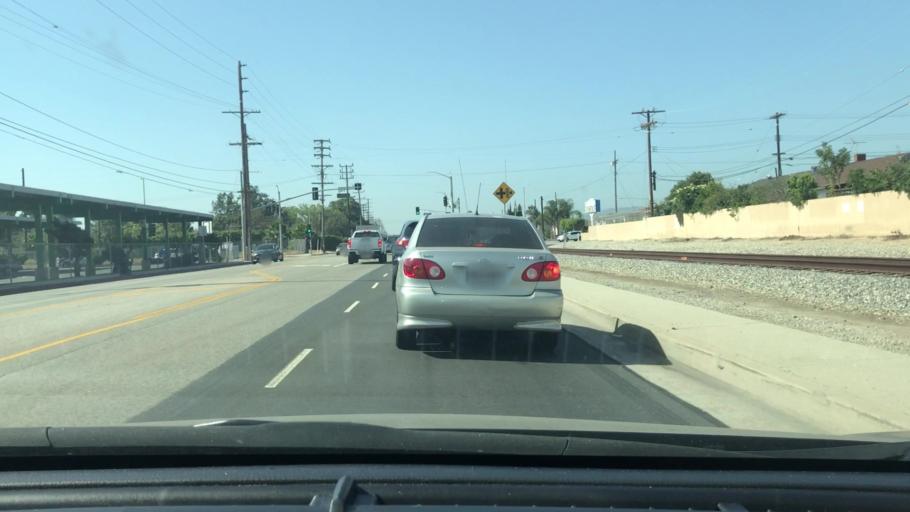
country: US
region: California
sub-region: Los Angeles County
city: Gardena
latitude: 33.8669
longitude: -118.2992
